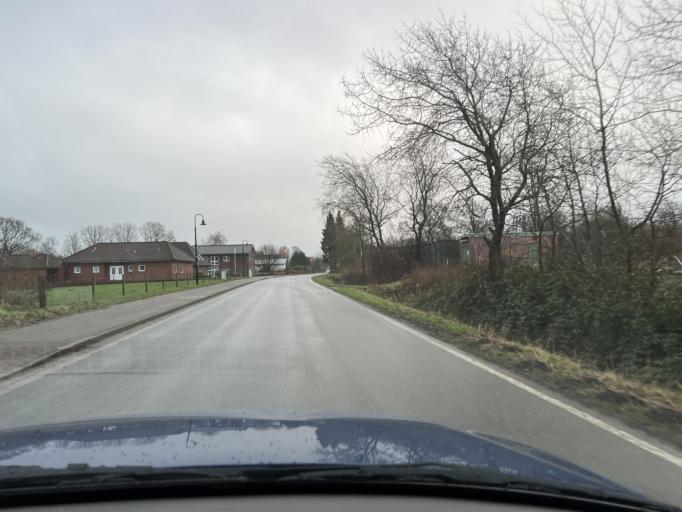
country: DE
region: Schleswig-Holstein
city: Lohe-Rickelshof
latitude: 54.2126
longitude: 9.0728
